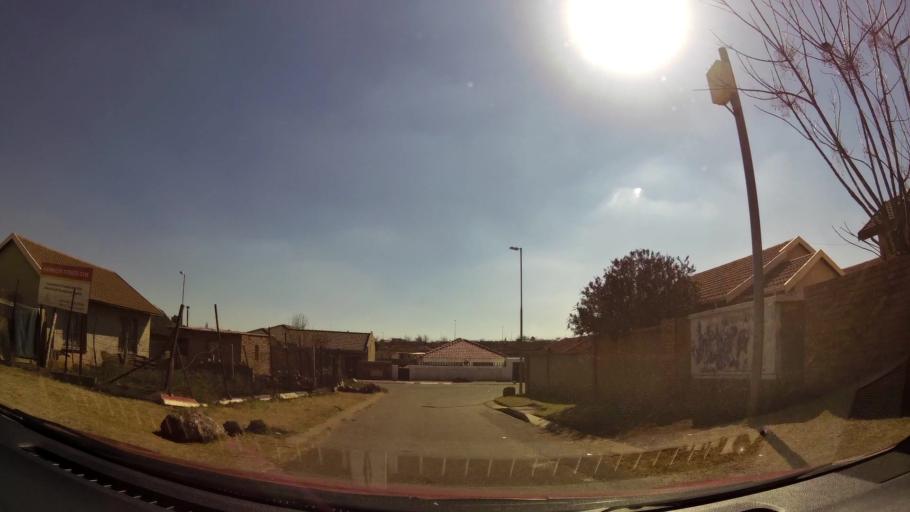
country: ZA
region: Gauteng
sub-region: City of Johannesburg Metropolitan Municipality
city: Soweto
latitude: -26.2331
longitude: 27.8228
